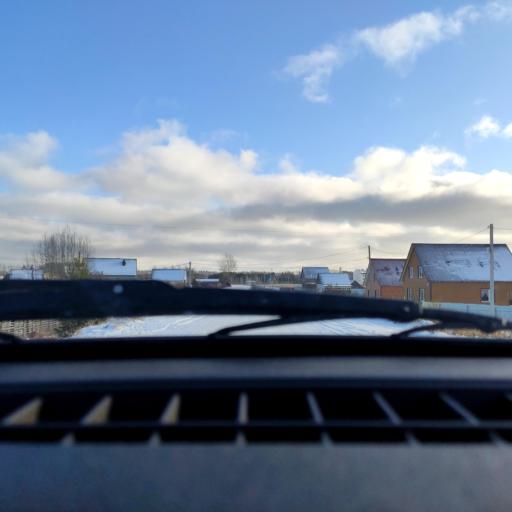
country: RU
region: Bashkortostan
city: Iglino
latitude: 54.8054
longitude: 56.4058
